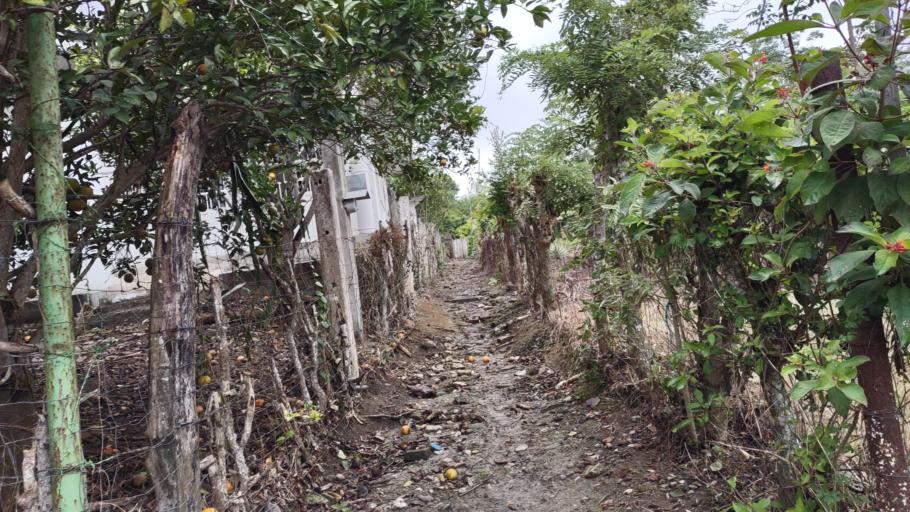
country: MX
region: Veracruz
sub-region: Papantla
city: El Chote
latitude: 20.4127
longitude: -97.3672
